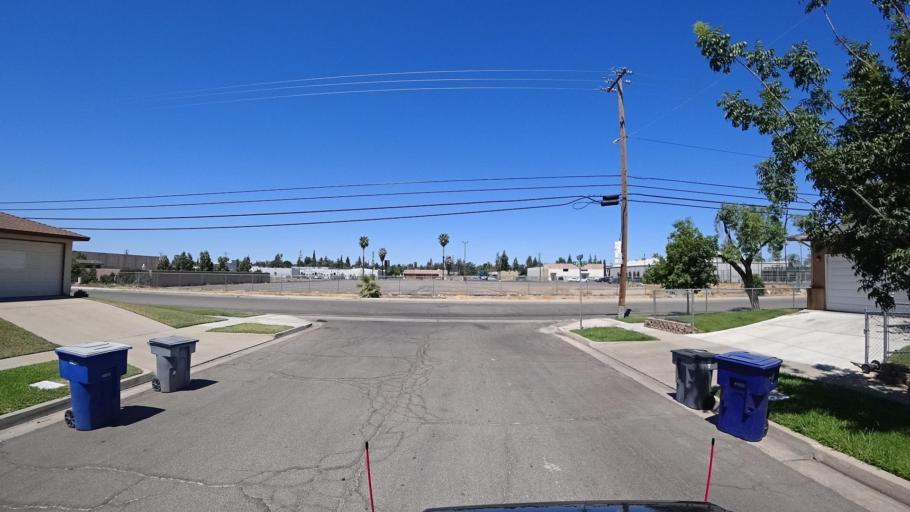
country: US
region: California
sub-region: Fresno County
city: Fresno
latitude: 36.8035
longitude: -119.7879
